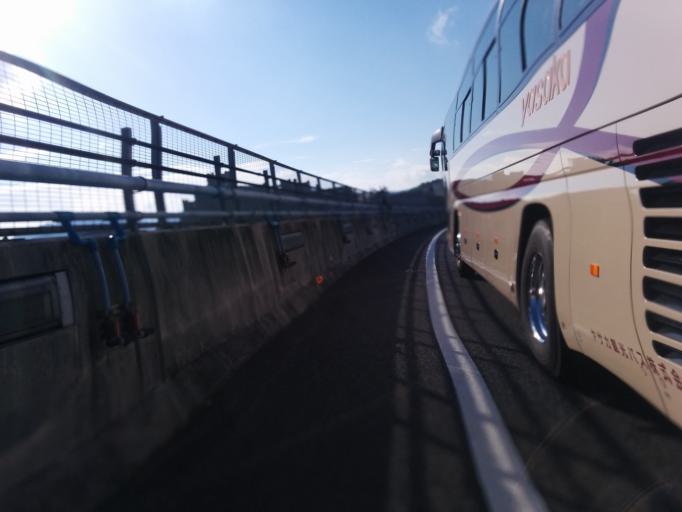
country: JP
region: Shiga Prefecture
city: Kusatsu
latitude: 34.9824
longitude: 135.9584
